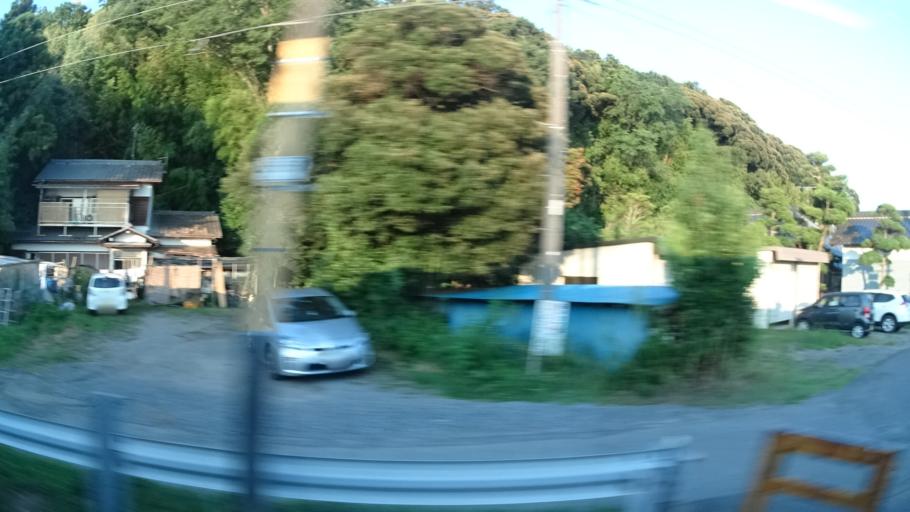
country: JP
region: Ibaraki
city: Ushiku
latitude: 35.9410
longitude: 140.1383
